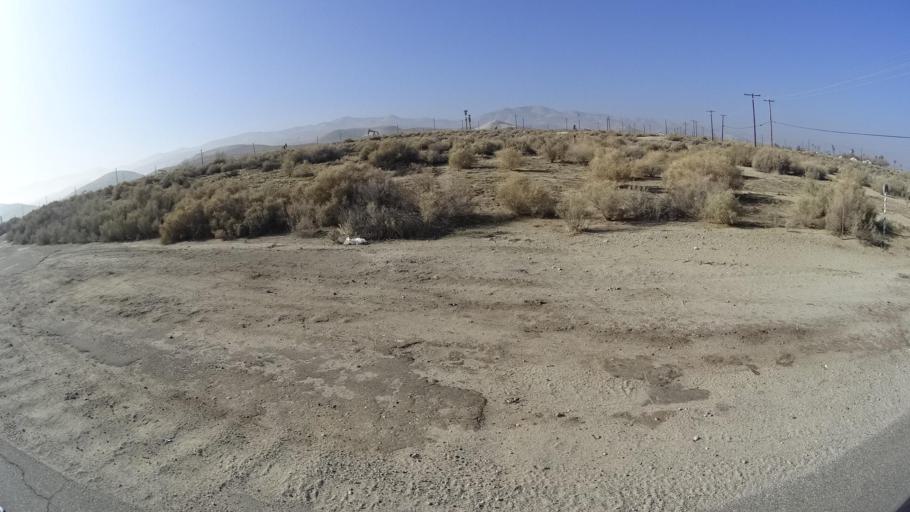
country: US
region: California
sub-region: Kern County
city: Taft Heights
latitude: 35.1801
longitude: -119.5495
